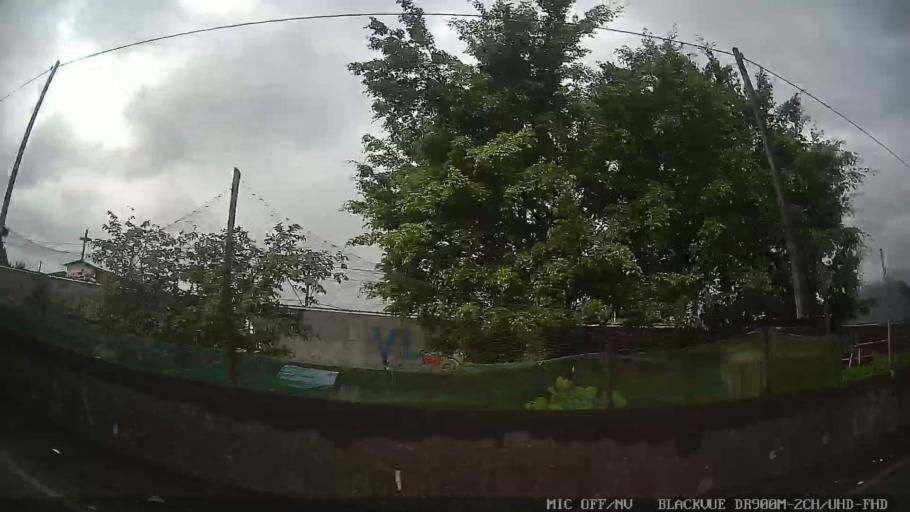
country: BR
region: Sao Paulo
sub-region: Cubatao
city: Cubatao
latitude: -23.8991
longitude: -46.4474
